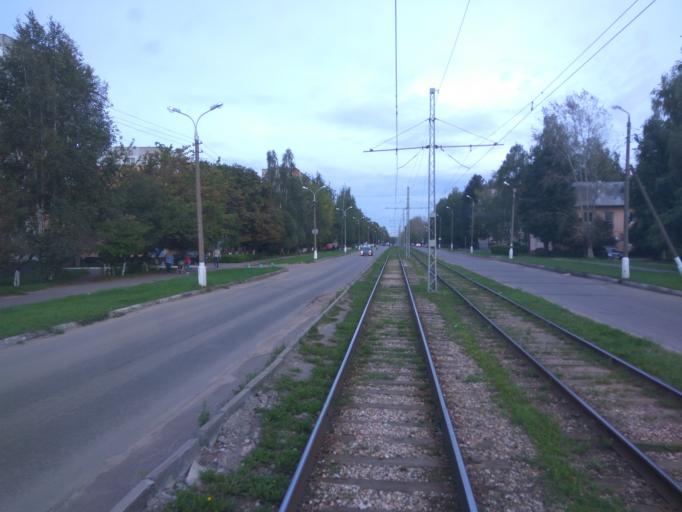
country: RU
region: Moskovskaya
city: Kolomna
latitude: 55.0782
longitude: 38.7716
